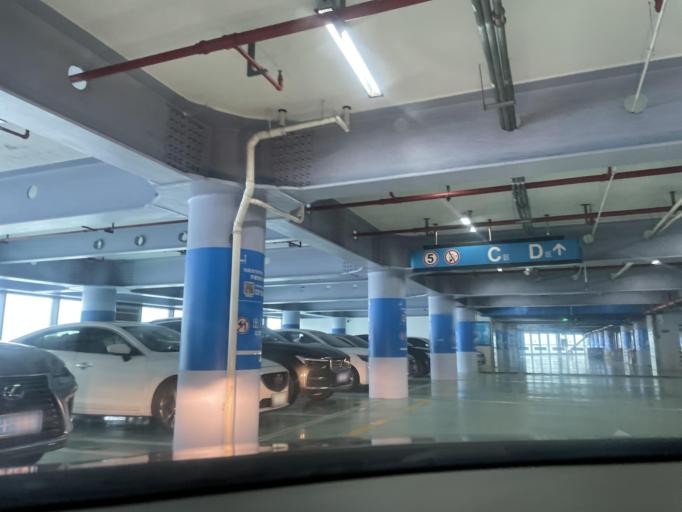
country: CN
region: Zhejiang Sheng
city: Zhapu
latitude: 30.4629
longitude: 121.1247
